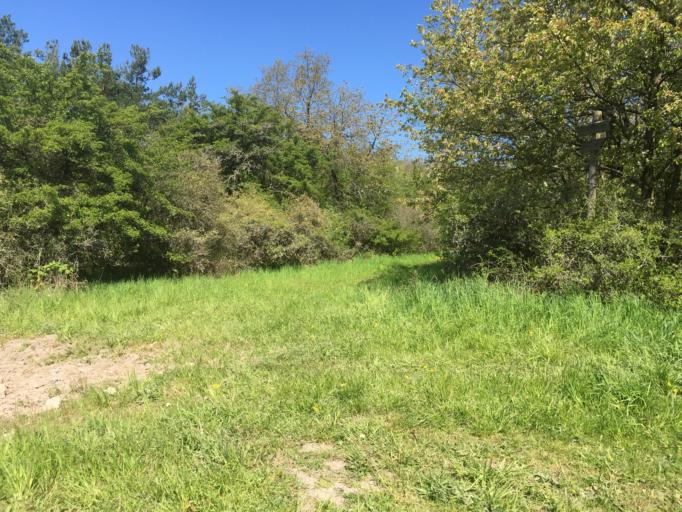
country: DE
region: Bavaria
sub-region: Regierungsbezirk Unterfranken
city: Sulzfeld
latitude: 50.2698
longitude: 10.4123
